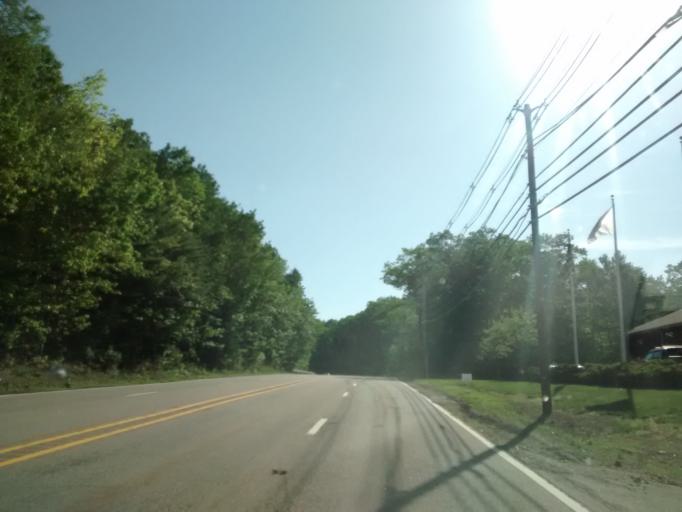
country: US
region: Massachusetts
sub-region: Worcester County
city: Sturbridge
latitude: 42.1354
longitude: -72.0372
